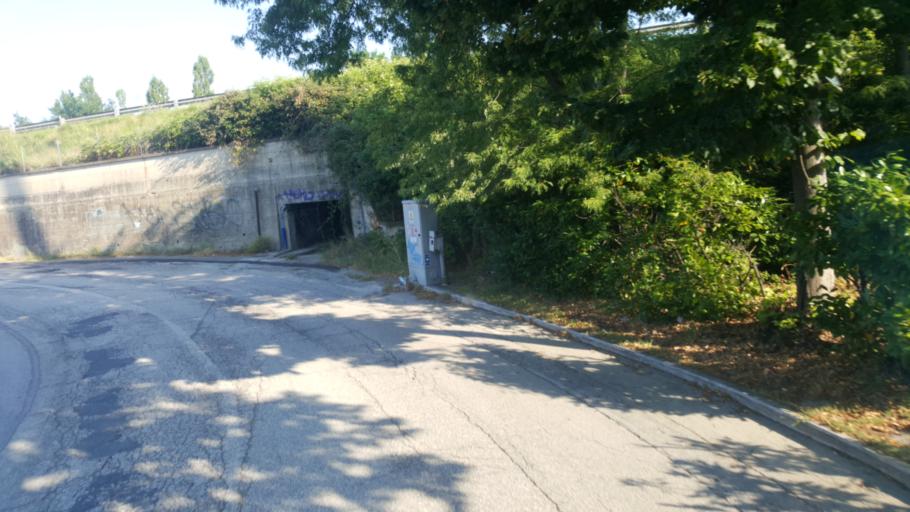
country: IT
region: Umbria
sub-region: Provincia di Perugia
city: Via Lippia
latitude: 43.0864
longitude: 12.4445
